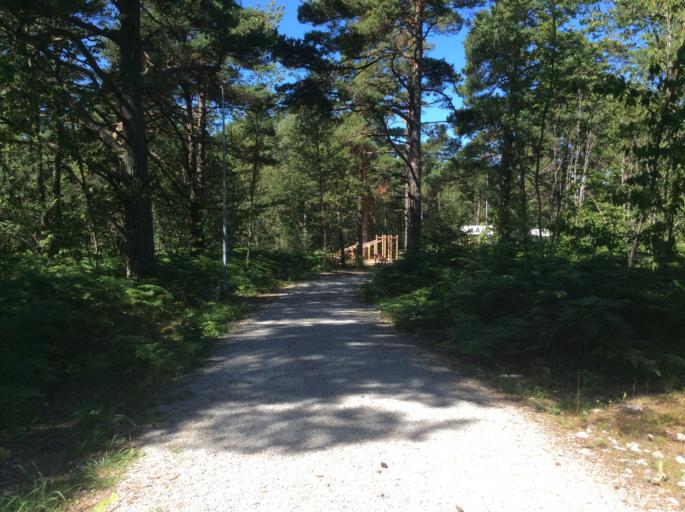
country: SE
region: Gotland
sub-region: Gotland
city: Vibble
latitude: 57.6051
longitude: 18.2802
